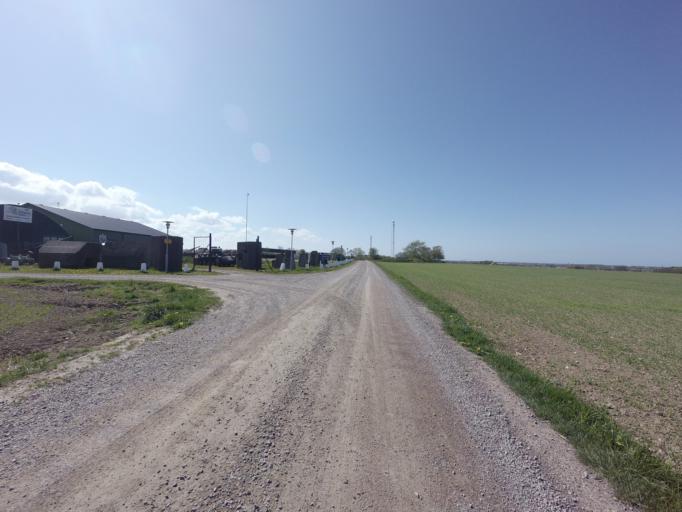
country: DK
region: Capital Region
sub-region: Helsingor Kommune
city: Helsingor
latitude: 56.1298
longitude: 12.6401
